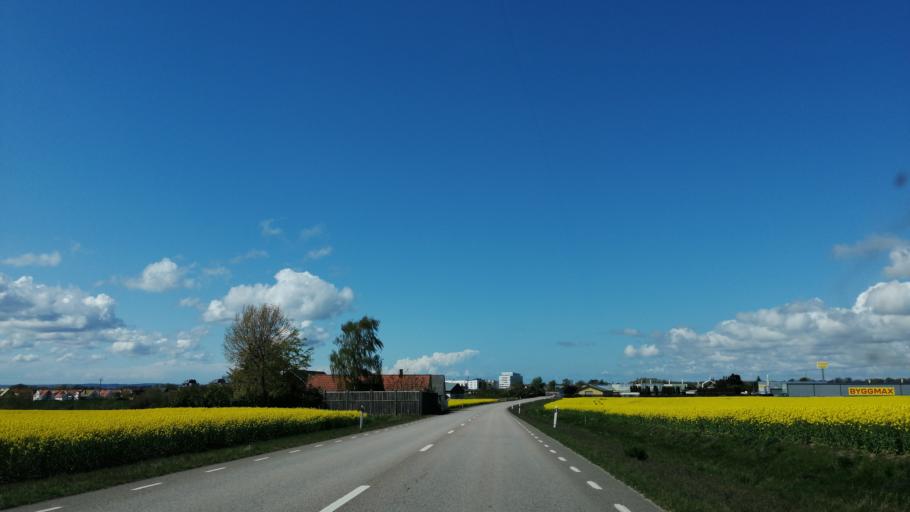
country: SE
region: Skane
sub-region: Helsingborg
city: Gantofta
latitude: 55.9594
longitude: 12.7914
